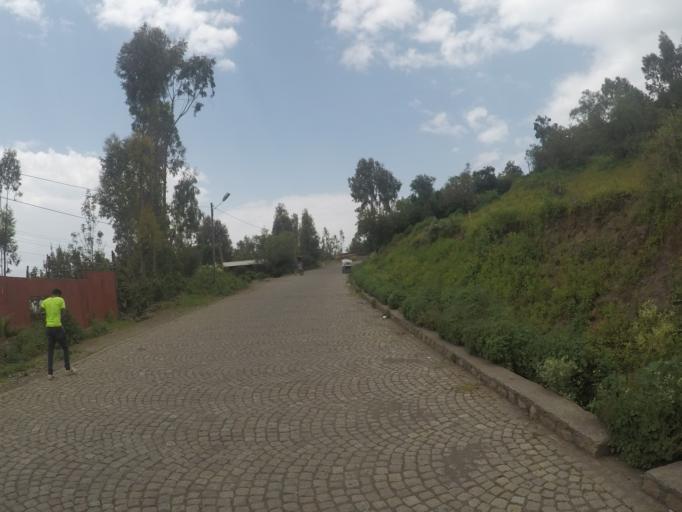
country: ET
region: Amhara
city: Lalibela
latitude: 12.0298
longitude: 39.0464
